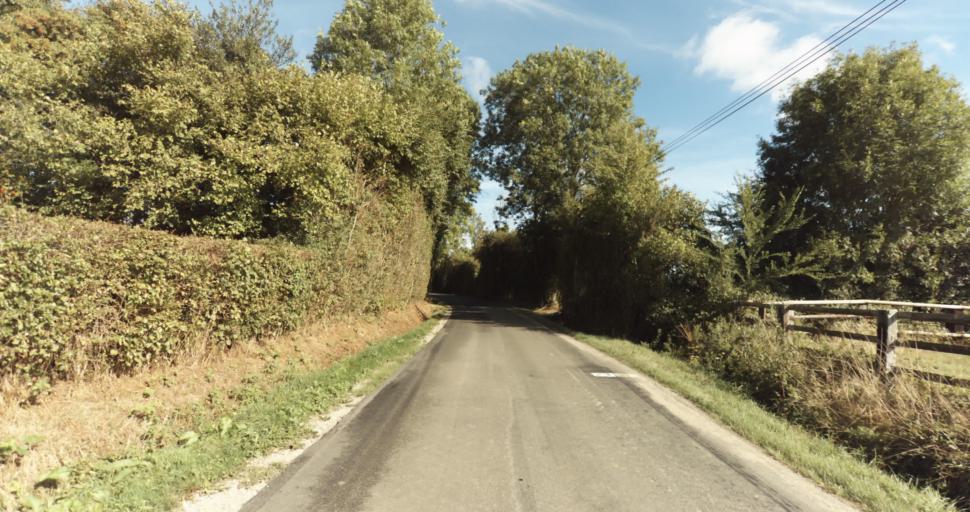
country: FR
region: Lower Normandy
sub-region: Departement du Calvados
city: La Vespiere
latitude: 48.9344
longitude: 0.3455
